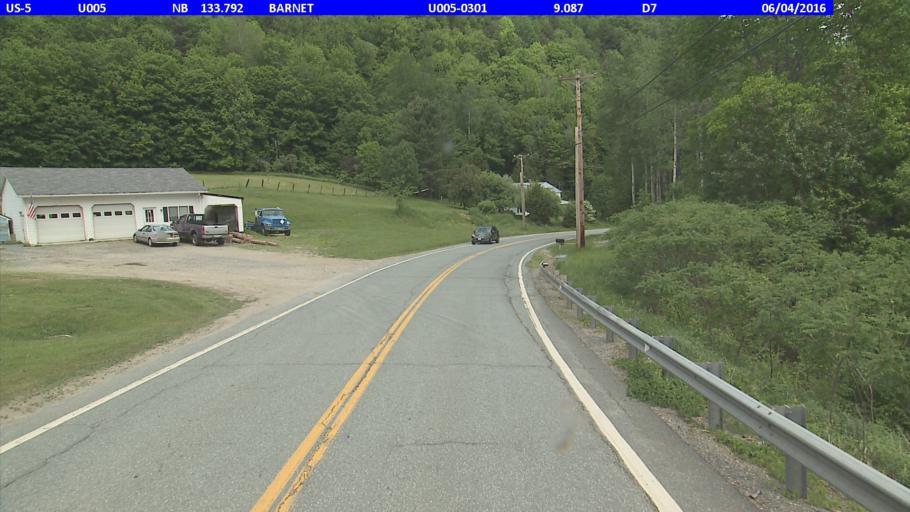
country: US
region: Vermont
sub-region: Caledonia County
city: Saint Johnsbury
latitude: 44.3703
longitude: -72.0357
